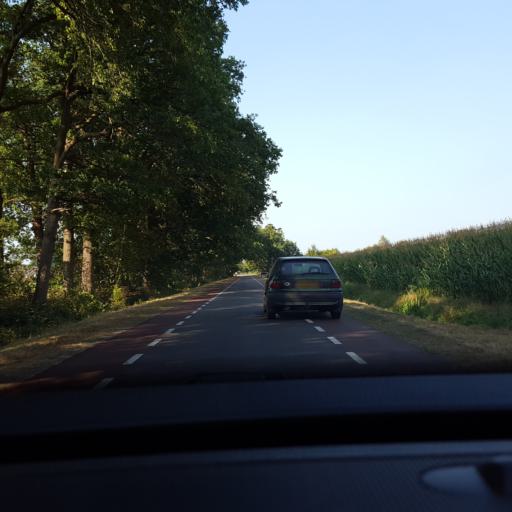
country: NL
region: Gelderland
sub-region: Gemeente Lochem
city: Barchem
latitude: 52.0610
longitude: 6.4544
